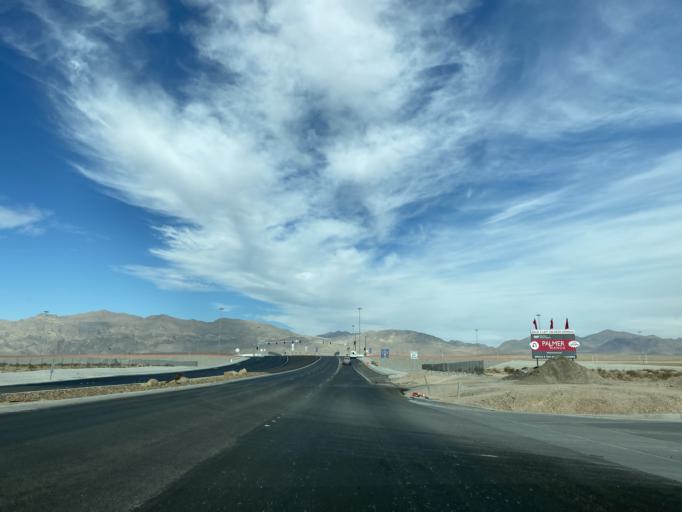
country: US
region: Nevada
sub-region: Clark County
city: Nellis Air Force Base
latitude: 36.2859
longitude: -115.1167
